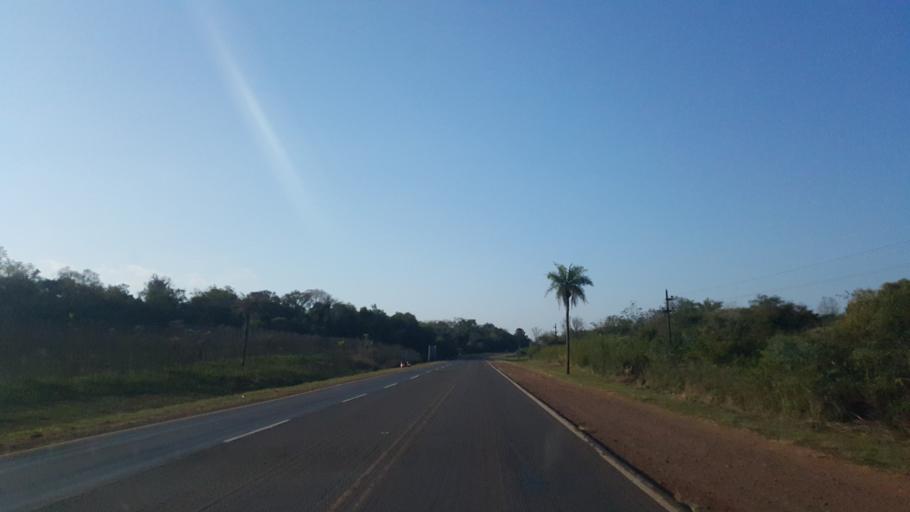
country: AR
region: Misiones
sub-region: Departamento de Candelaria
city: Loreto
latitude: -27.3358
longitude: -55.5442
